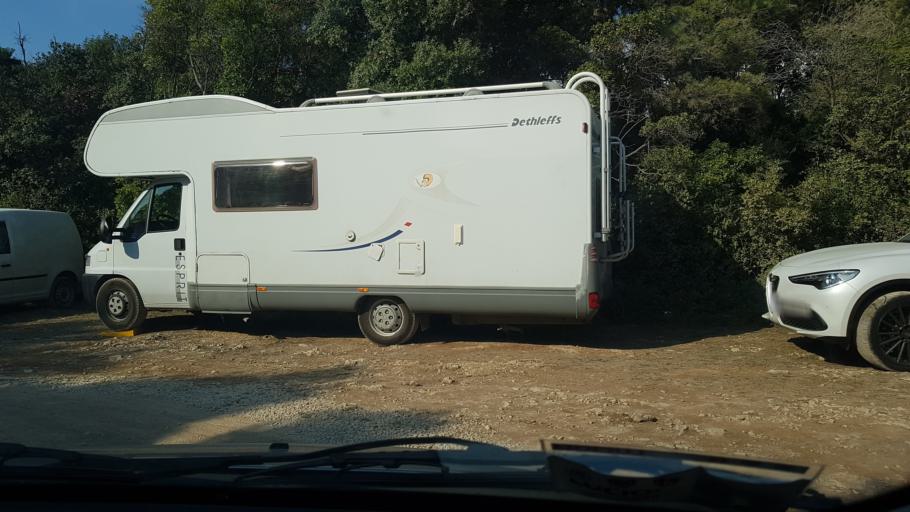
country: HR
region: Istarska
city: Vrsar
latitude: 45.1139
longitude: 13.6104
